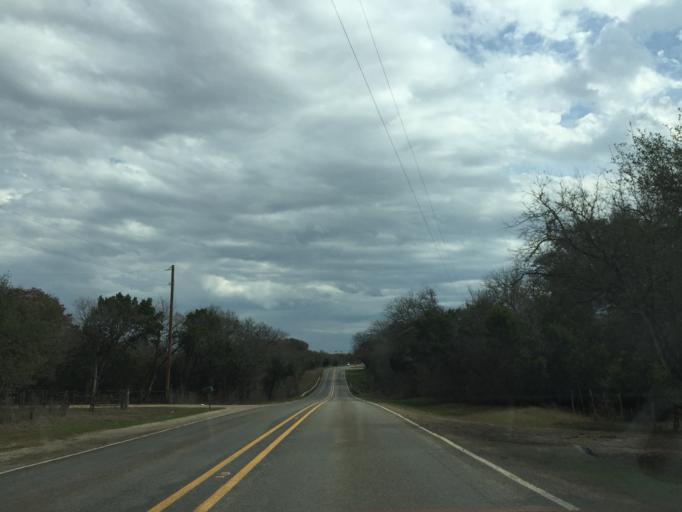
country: US
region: Texas
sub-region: Williamson County
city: Leander
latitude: 30.6603
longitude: -97.9442
